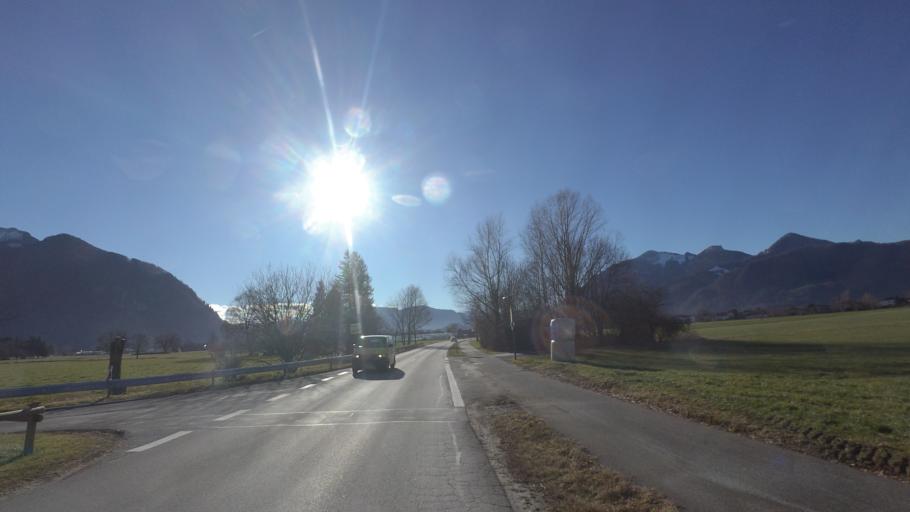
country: DE
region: Bavaria
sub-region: Upper Bavaria
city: Staudach-Egerndach
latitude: 47.7901
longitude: 12.4695
